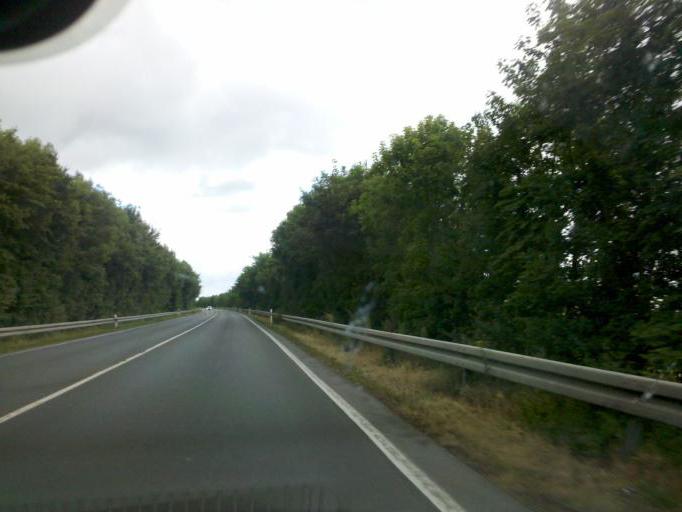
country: DE
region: North Rhine-Westphalia
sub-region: Regierungsbezirk Arnsberg
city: Anrochte
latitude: 51.5587
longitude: 8.3057
